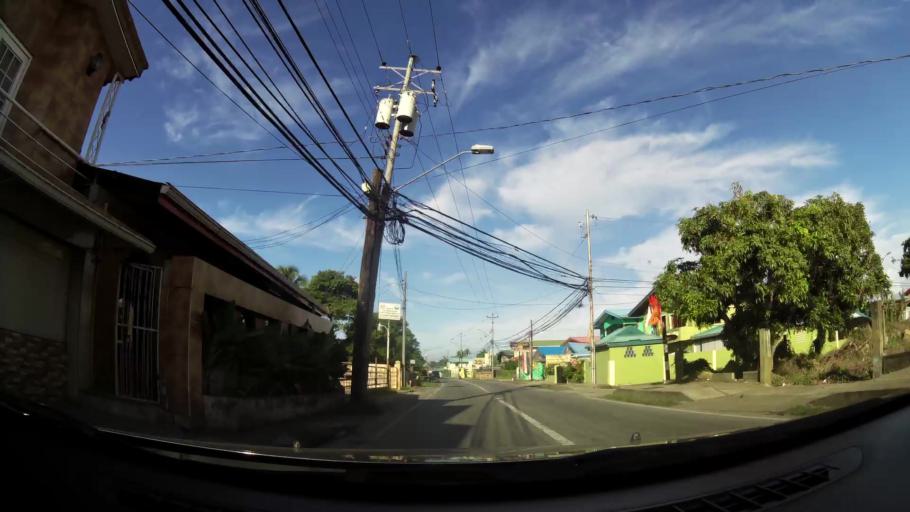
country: TT
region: Chaguanas
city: Chaguanas
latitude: 10.5471
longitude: -61.3492
